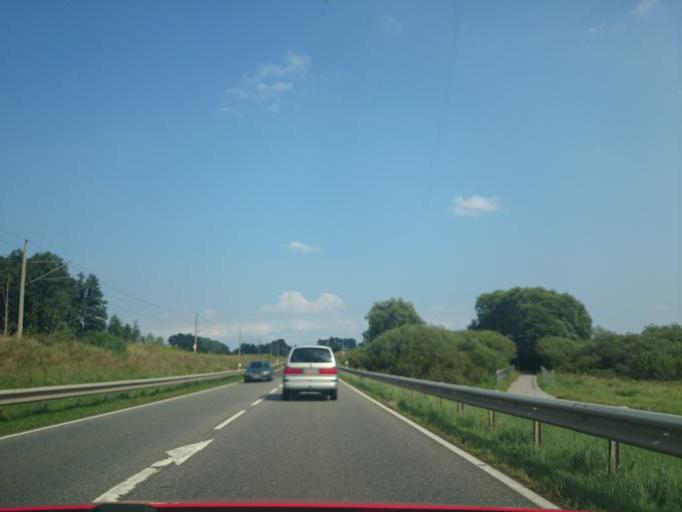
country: DE
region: Mecklenburg-Vorpommern
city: Preetz
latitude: 54.3027
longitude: 12.9961
